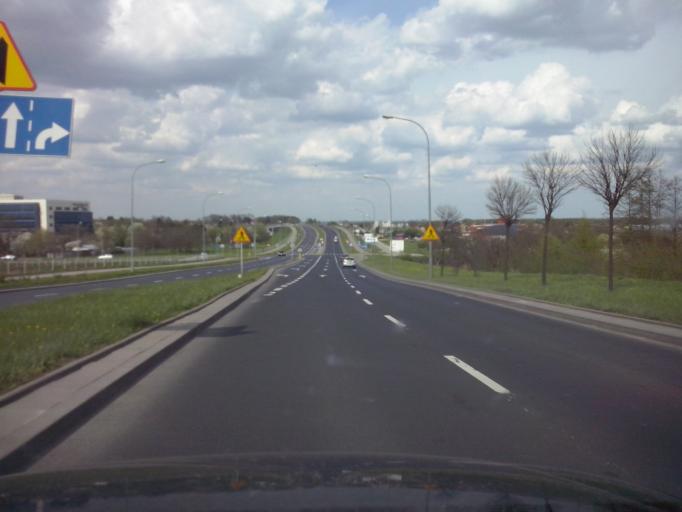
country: PL
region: Subcarpathian Voivodeship
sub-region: Powiat rzeszowski
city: Trzebownisko
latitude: 50.0479
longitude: 22.0335
